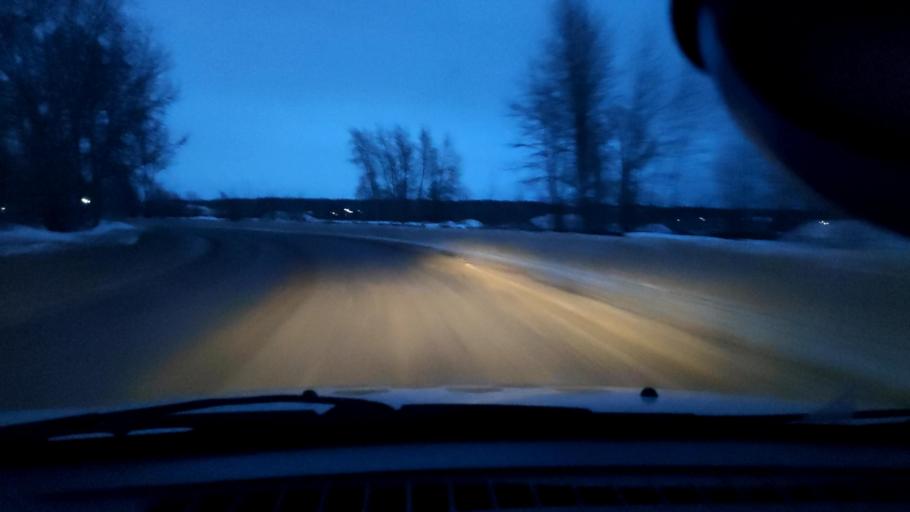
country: RU
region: Perm
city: Overyata
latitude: 58.0027
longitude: 55.9107
